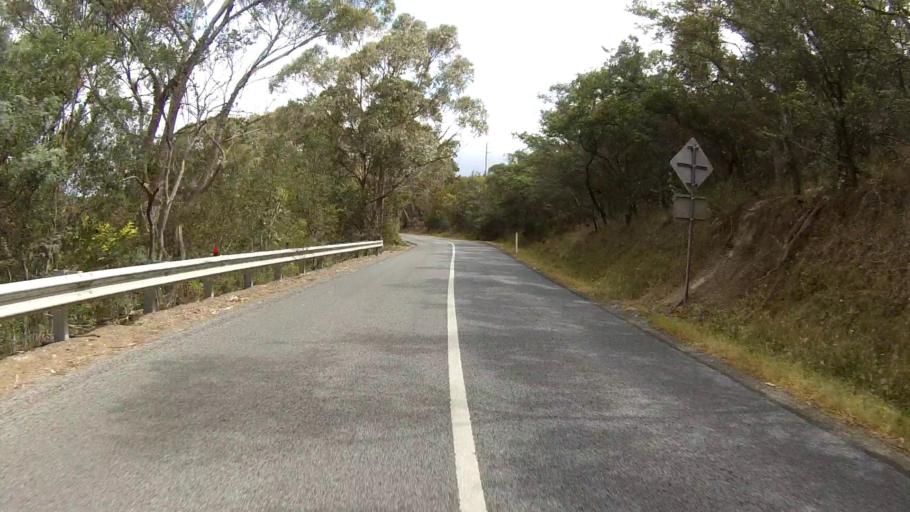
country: AU
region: Tasmania
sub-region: Clarence
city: Howrah
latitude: -42.8564
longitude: 147.4199
